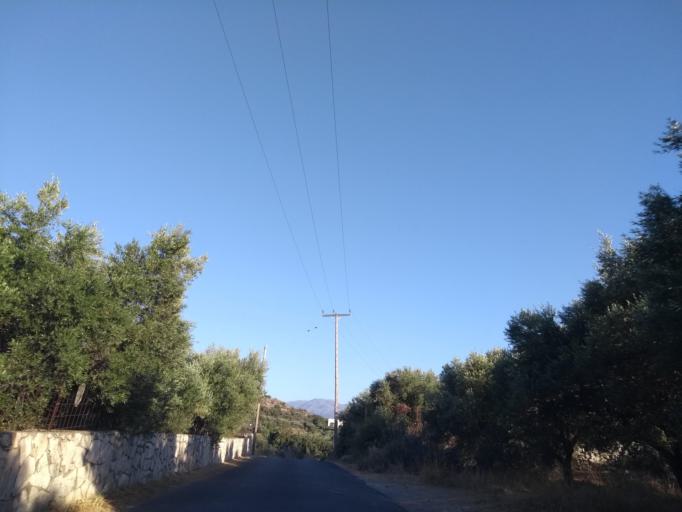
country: GR
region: Crete
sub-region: Nomos Chanias
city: Kalivai
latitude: 35.4343
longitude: 24.1752
